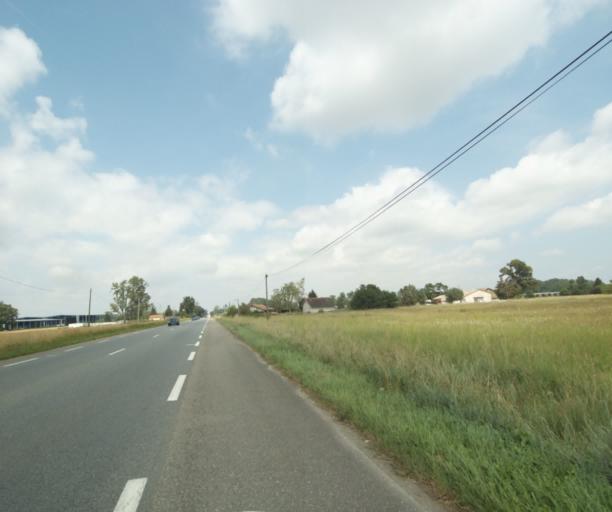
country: FR
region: Midi-Pyrenees
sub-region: Departement du Tarn-et-Garonne
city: Albias
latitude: 44.0637
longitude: 1.4136
